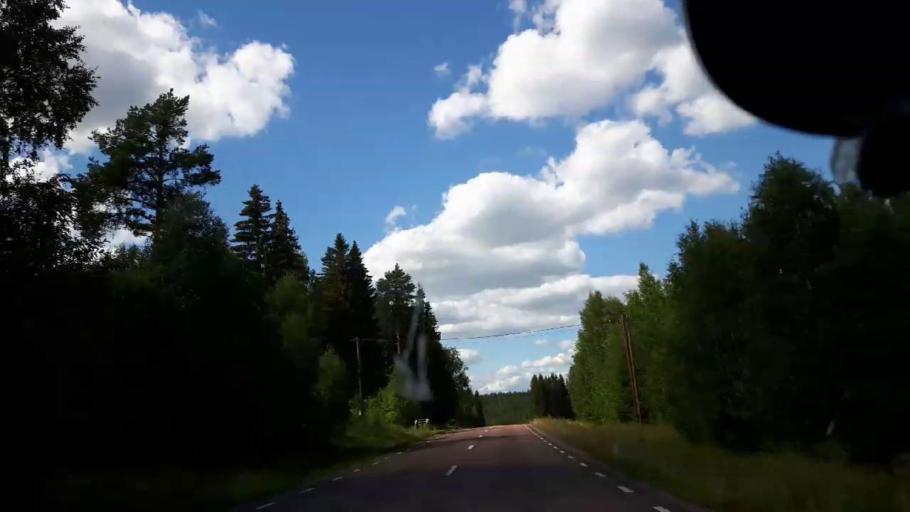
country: SE
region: Jaemtland
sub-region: Ragunda Kommun
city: Hammarstrand
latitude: 63.0196
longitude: 16.5561
